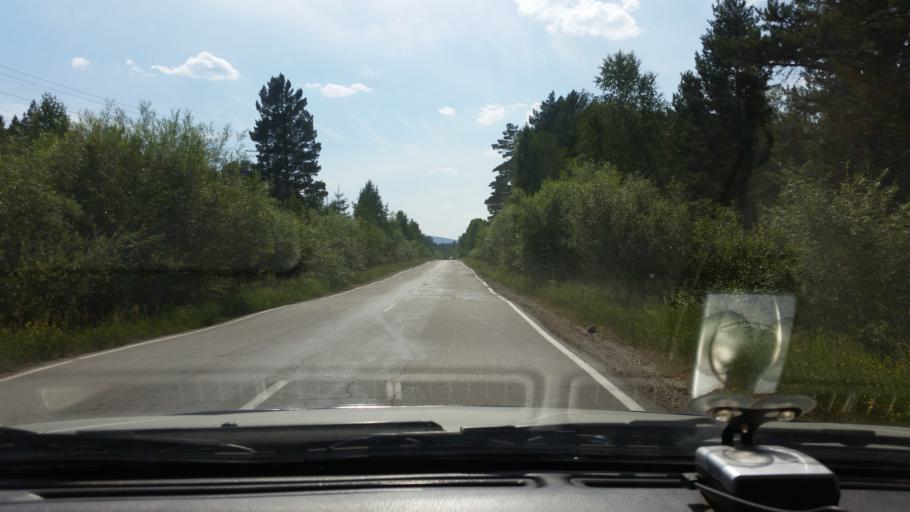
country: RU
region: Irkutsk
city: Baklashi
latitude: 52.2126
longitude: 103.9789
